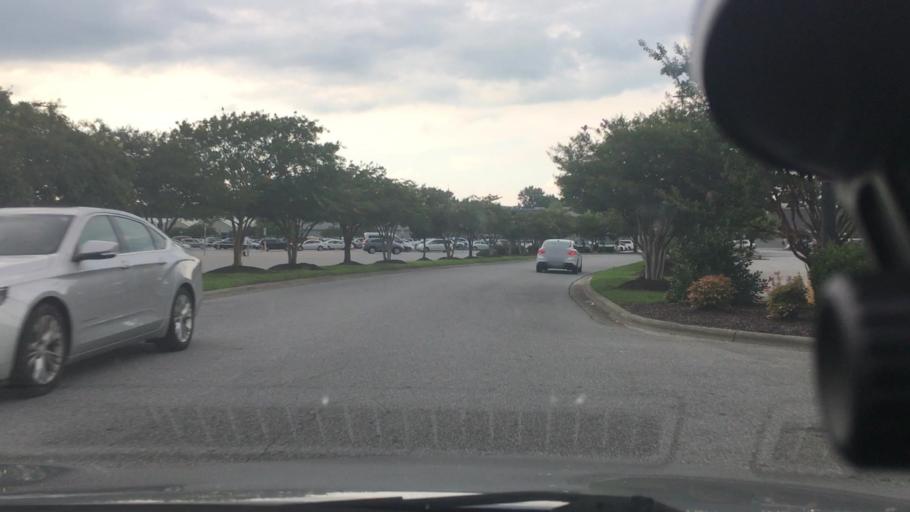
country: US
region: North Carolina
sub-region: Pitt County
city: Summerfield
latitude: 35.5753
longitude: -77.3873
